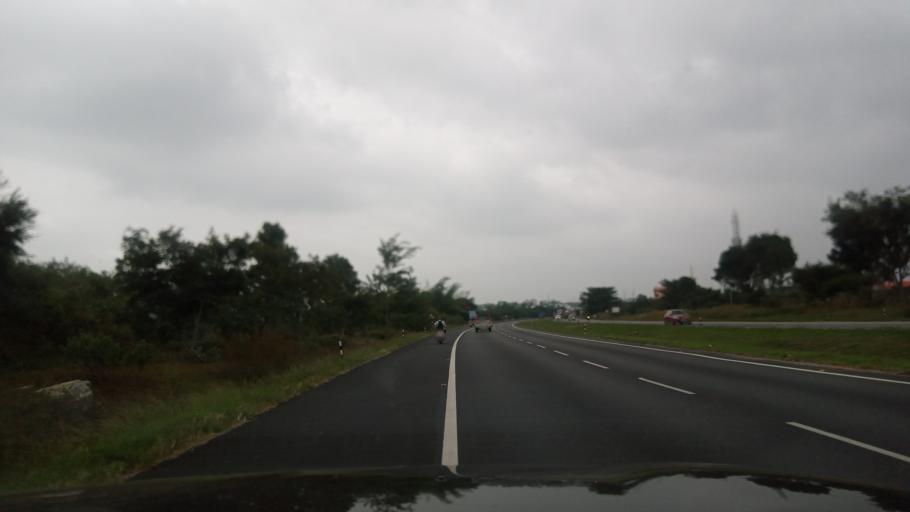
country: IN
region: Karnataka
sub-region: Bangalore Urban
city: Bangalore
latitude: 12.8646
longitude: 77.6261
